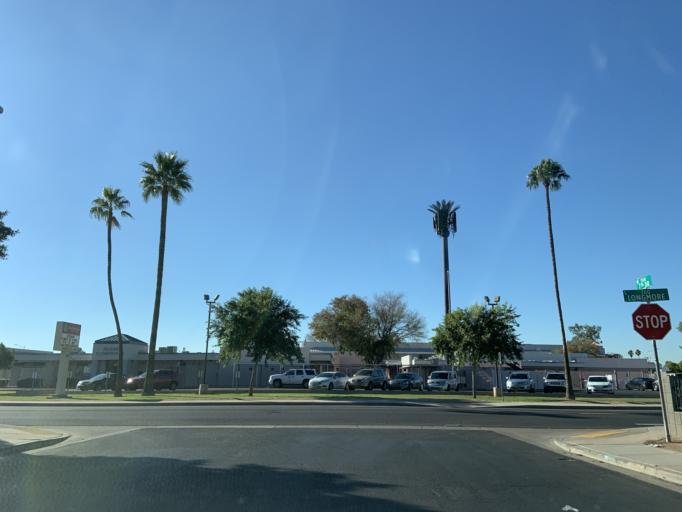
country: US
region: Arizona
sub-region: Maricopa County
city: Tempe
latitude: 33.4015
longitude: -111.8656
